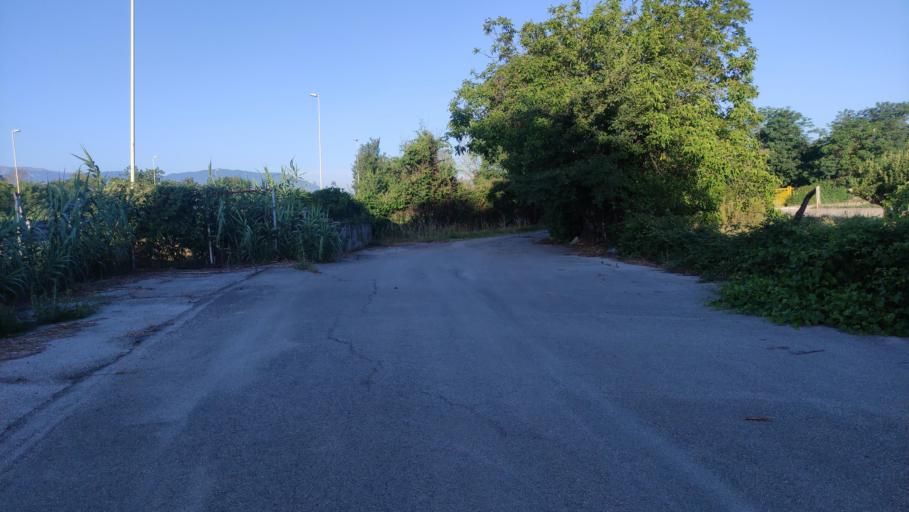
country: IT
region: Abruzzo
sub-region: Provincia di Pescara
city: Manoppello Scalo
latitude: 42.3251
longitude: 14.0849
